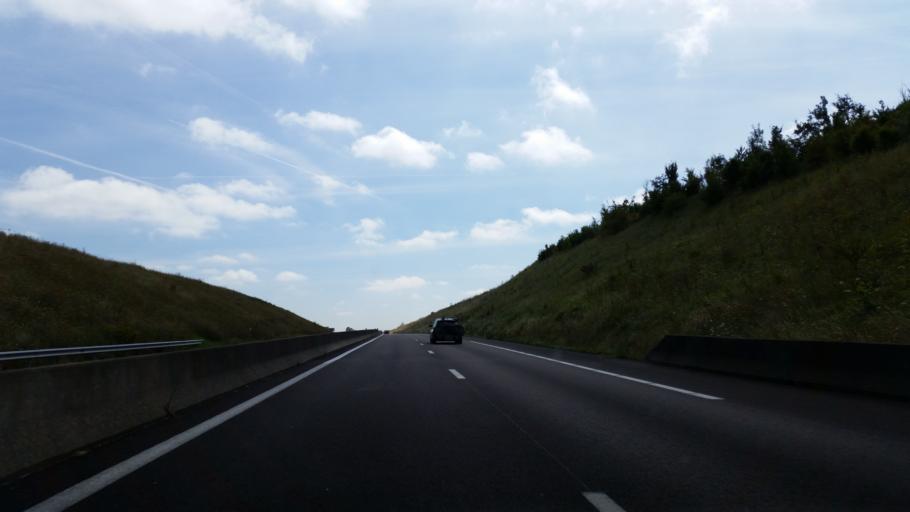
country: FR
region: Haute-Normandie
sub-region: Departement de la Seine-Maritime
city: Neufchatel-en-Bray
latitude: 49.7500
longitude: 1.5110
